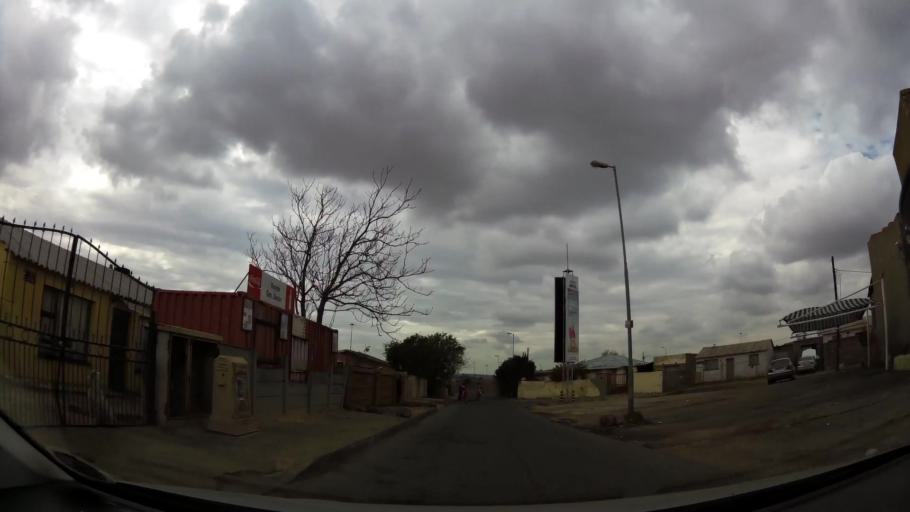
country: ZA
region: Gauteng
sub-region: City of Johannesburg Metropolitan Municipality
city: Soweto
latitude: -26.2690
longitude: 27.8641
